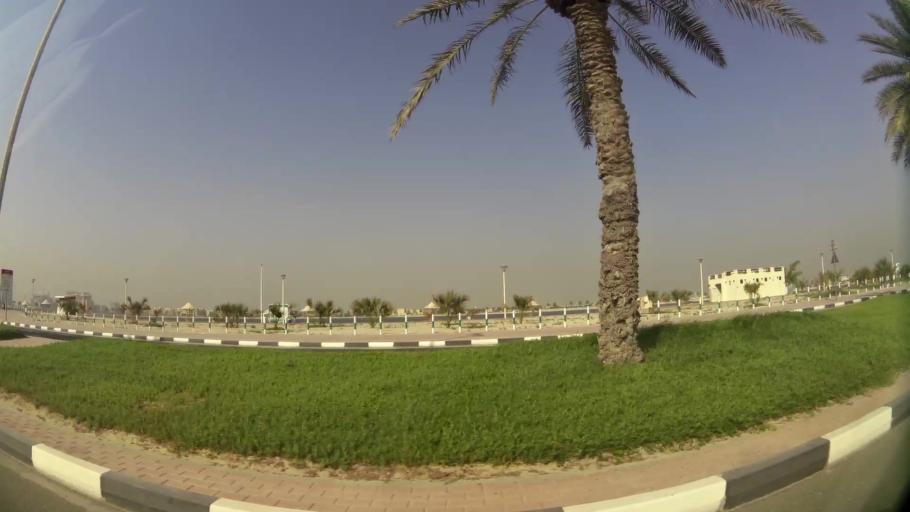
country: AE
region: Ash Shariqah
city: Sharjah
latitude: 25.3058
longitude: 55.3555
